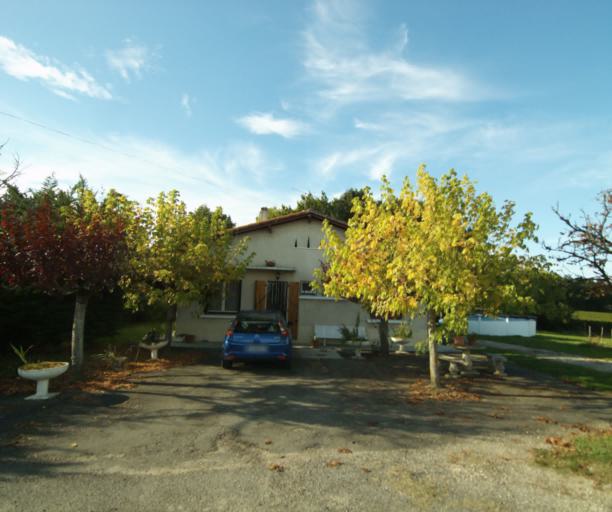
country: FR
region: Midi-Pyrenees
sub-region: Departement du Gers
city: Eauze
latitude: 43.8622
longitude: 0.0600
